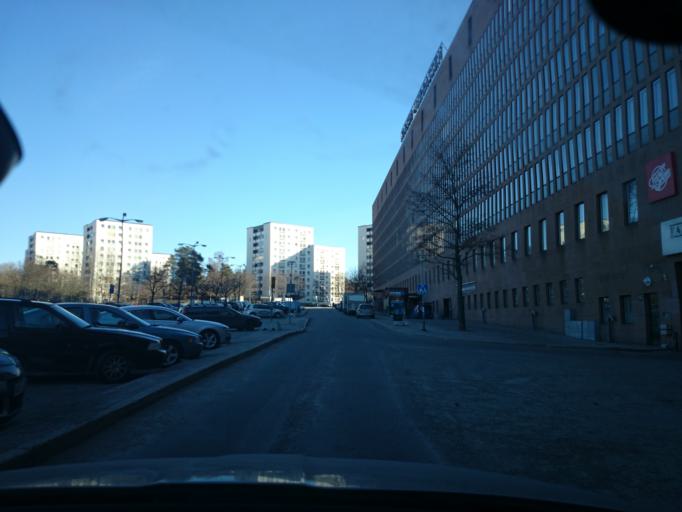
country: SE
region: Stockholm
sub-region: Stockholms Kommun
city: Arsta
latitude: 59.2426
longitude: 18.0937
